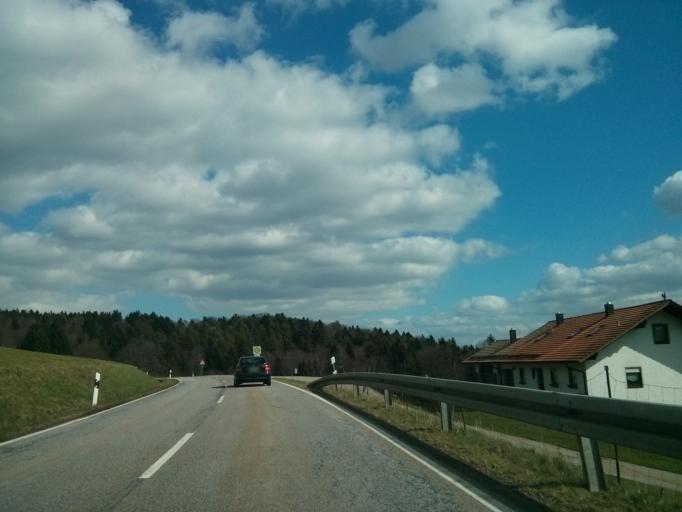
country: DE
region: Bavaria
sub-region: Lower Bavaria
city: Schaufling
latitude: 48.8415
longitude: 13.0363
